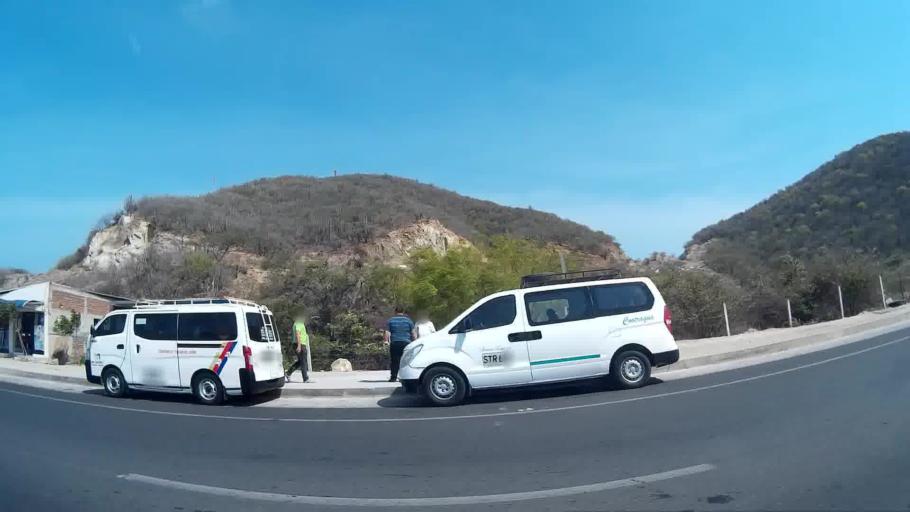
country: CO
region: Magdalena
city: Santa Marta
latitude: 11.1784
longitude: -74.2298
